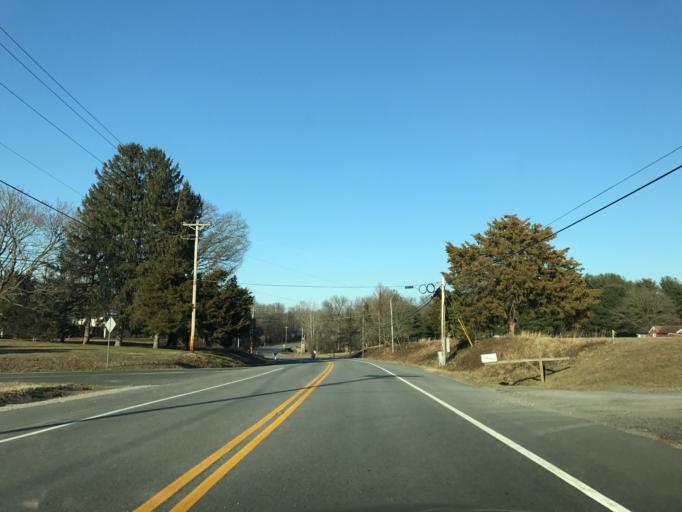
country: US
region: Maryland
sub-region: Queen Anne's County
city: Kingstown
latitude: 39.2476
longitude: -75.8630
